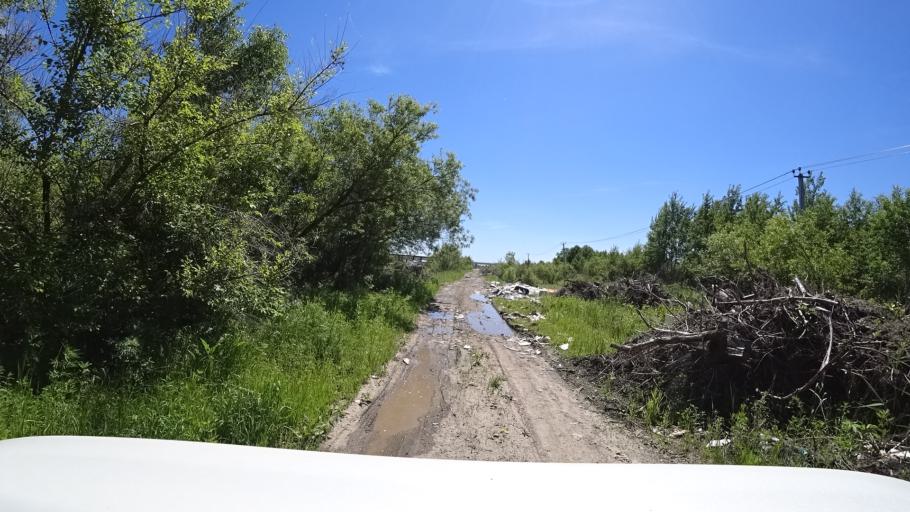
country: RU
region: Khabarovsk Krai
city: Topolevo
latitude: 48.4865
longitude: 135.1767
